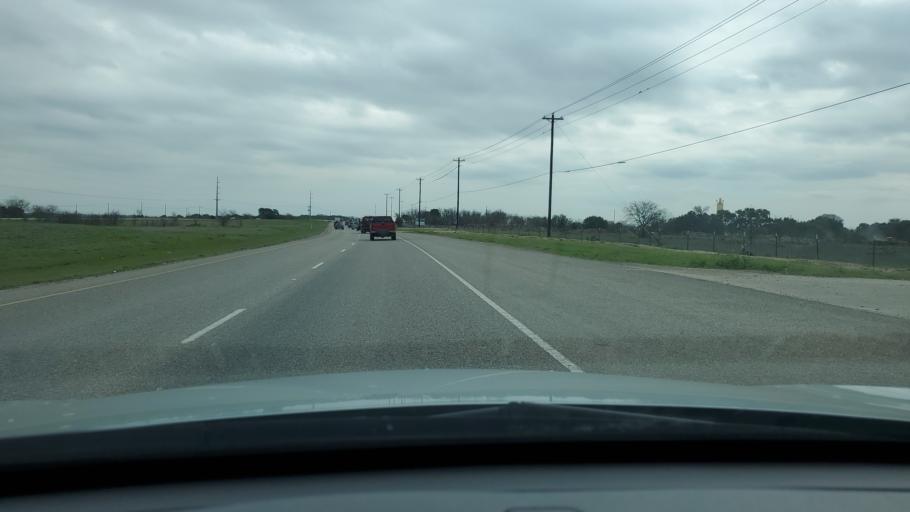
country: US
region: Texas
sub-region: Williamson County
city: Serenada
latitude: 30.7236
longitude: -97.6715
